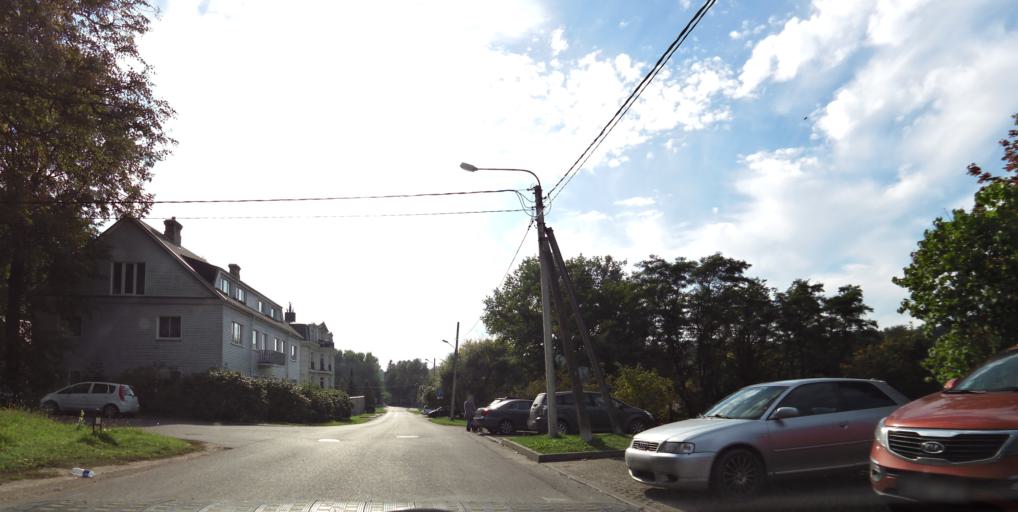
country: LT
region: Vilnius County
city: Seskine
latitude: 54.6913
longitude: 25.2463
